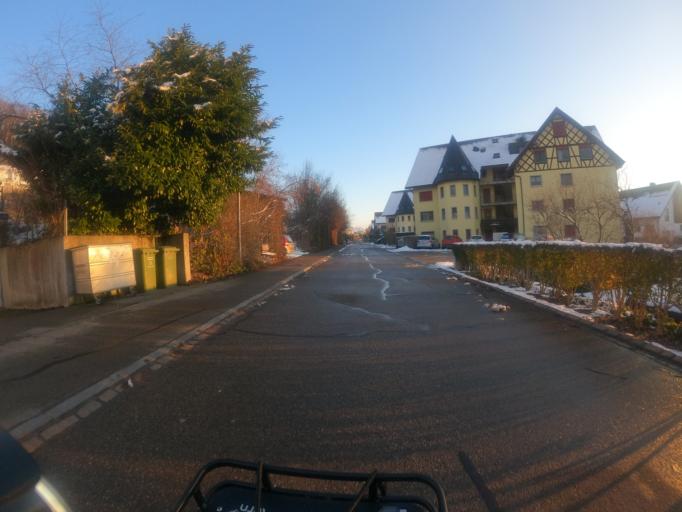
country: CH
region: Zurich
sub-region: Bezirk Affoltern
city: Hedingen
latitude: 47.2925
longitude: 8.4503
